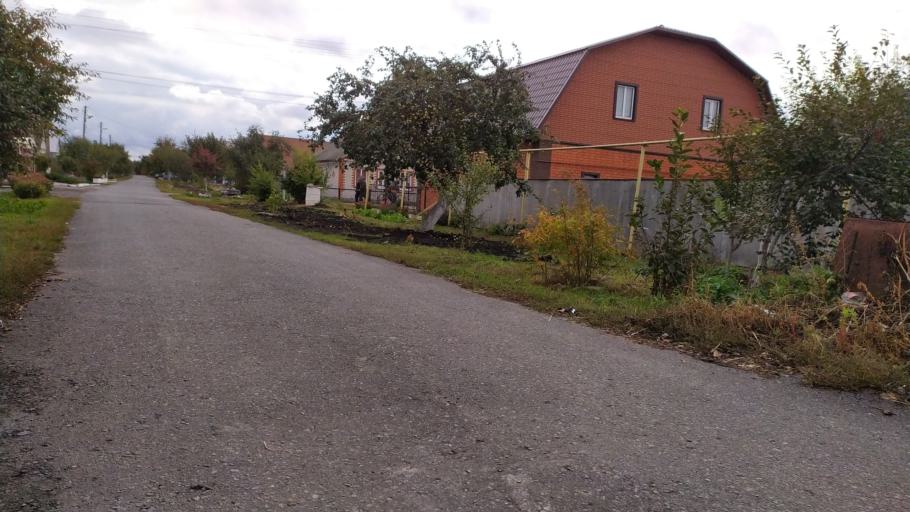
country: RU
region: Kursk
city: Kursk
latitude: 51.6459
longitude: 36.1515
